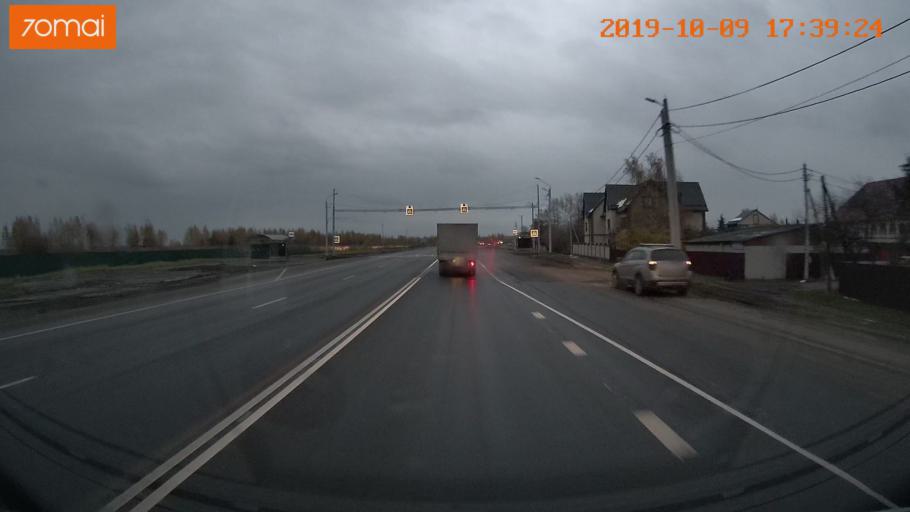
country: RU
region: Ivanovo
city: Bogorodskoye
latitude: 57.0609
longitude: 40.9581
